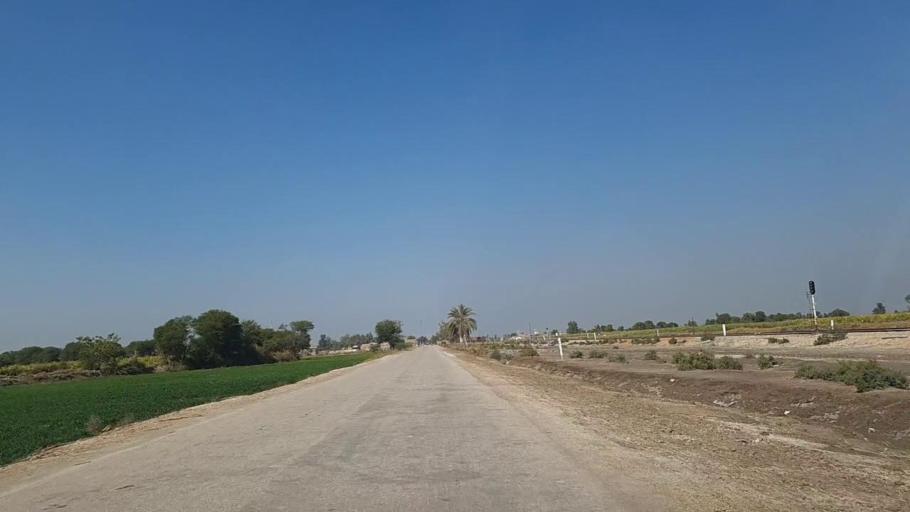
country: PK
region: Sindh
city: Nawabshah
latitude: 26.3440
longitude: 68.3693
